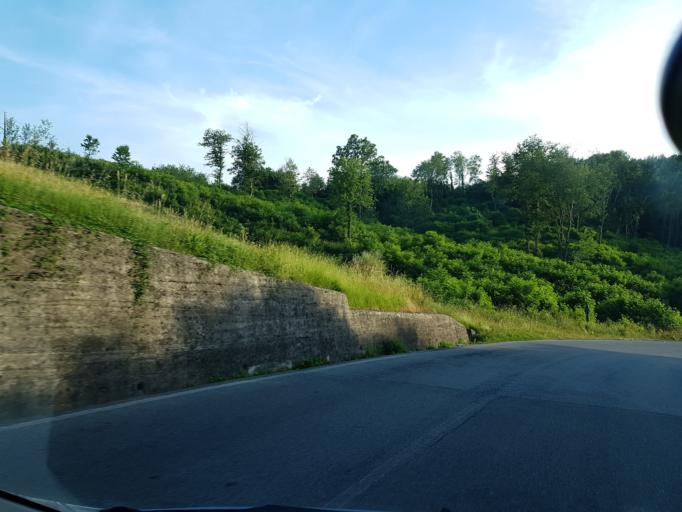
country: IT
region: Tuscany
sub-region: Provincia di Massa-Carrara
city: Fivizzano
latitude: 44.2057
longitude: 10.0819
